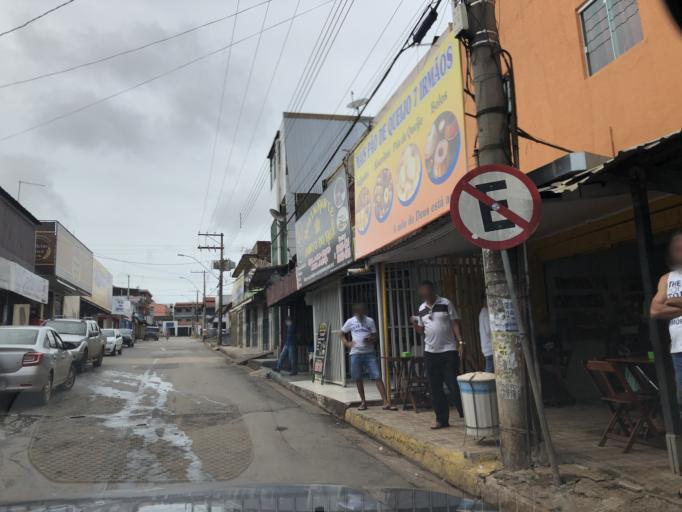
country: BR
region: Federal District
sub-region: Brasilia
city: Brasilia
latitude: -15.7831
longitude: -48.1395
